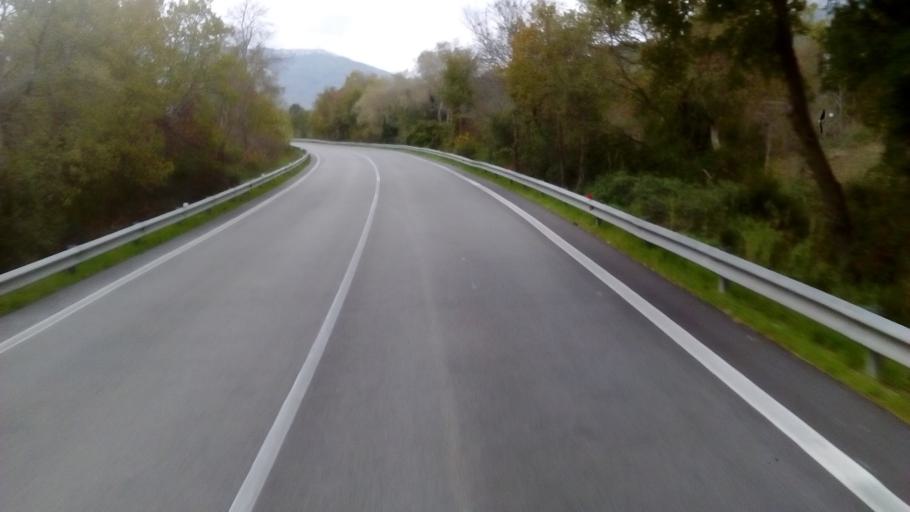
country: IT
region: Abruzzo
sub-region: Provincia di Chieti
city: Celenza sul Trigno
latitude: 41.8843
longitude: 14.6066
